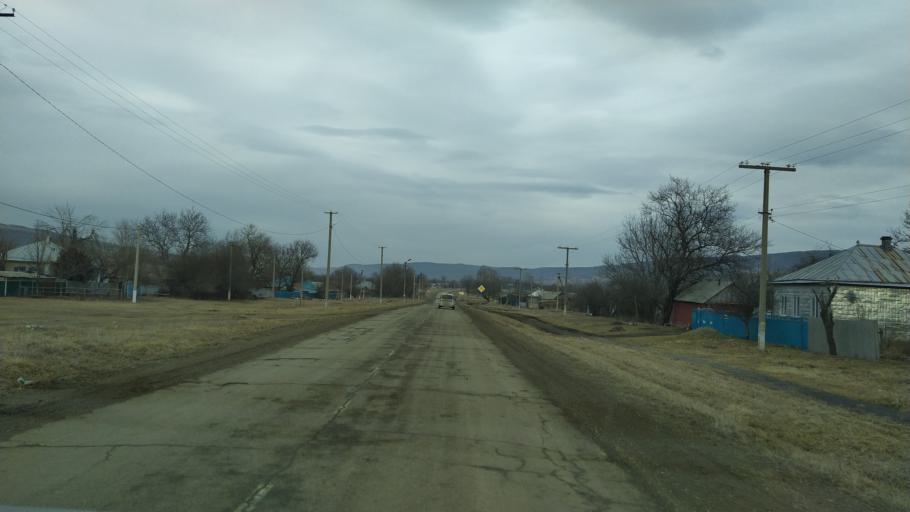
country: RU
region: Krasnodarskiy
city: Peredovaya
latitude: 44.1146
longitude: 41.4575
